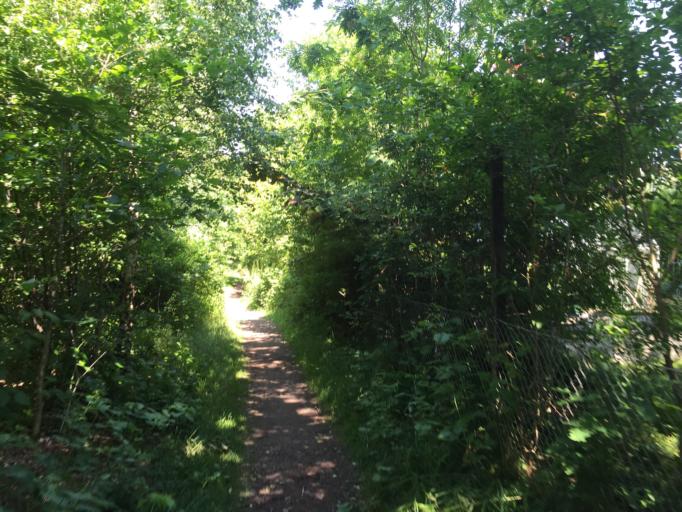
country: SE
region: Skane
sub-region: Lunds Kommun
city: Veberod
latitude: 55.6203
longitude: 13.5087
